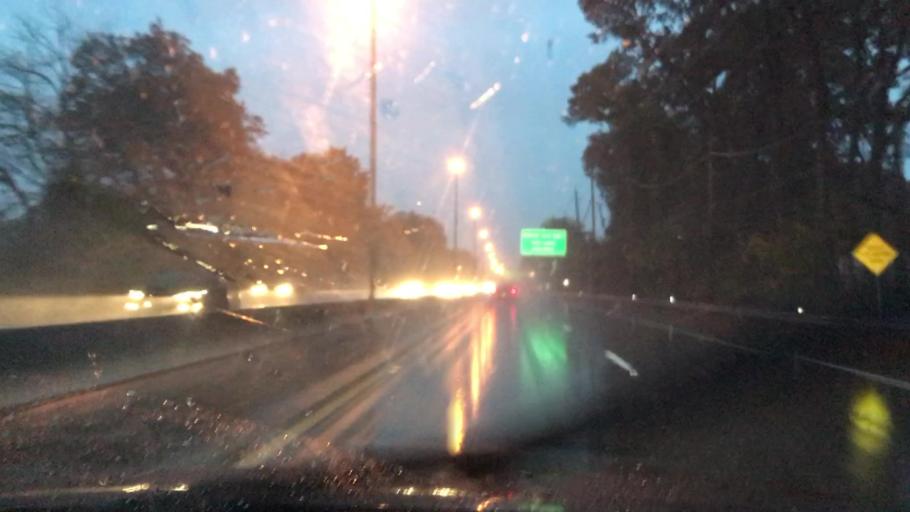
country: US
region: New Jersey
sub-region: Bergen County
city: Fair Lawn
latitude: 40.9303
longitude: -74.1065
